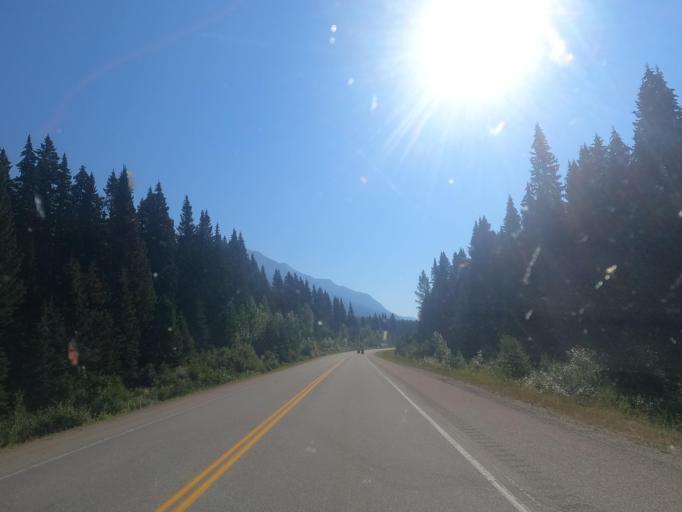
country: CA
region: Alberta
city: Grande Cache
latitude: 53.0016
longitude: -119.0361
